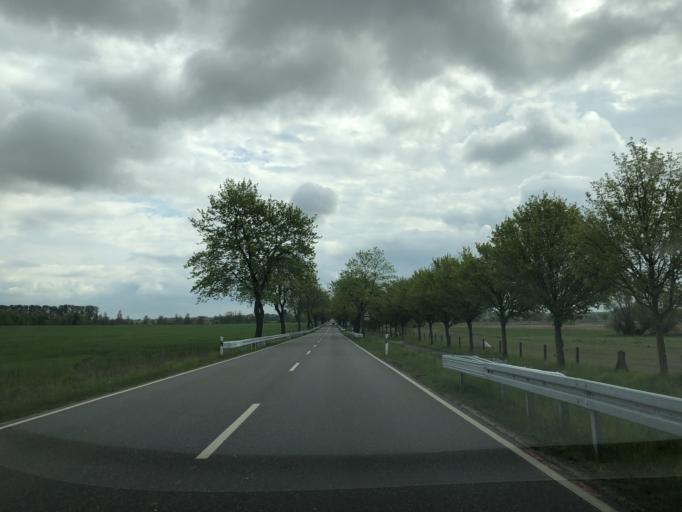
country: DE
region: Mecklenburg-Vorpommern
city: Lubz
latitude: 53.4658
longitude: 12.1138
